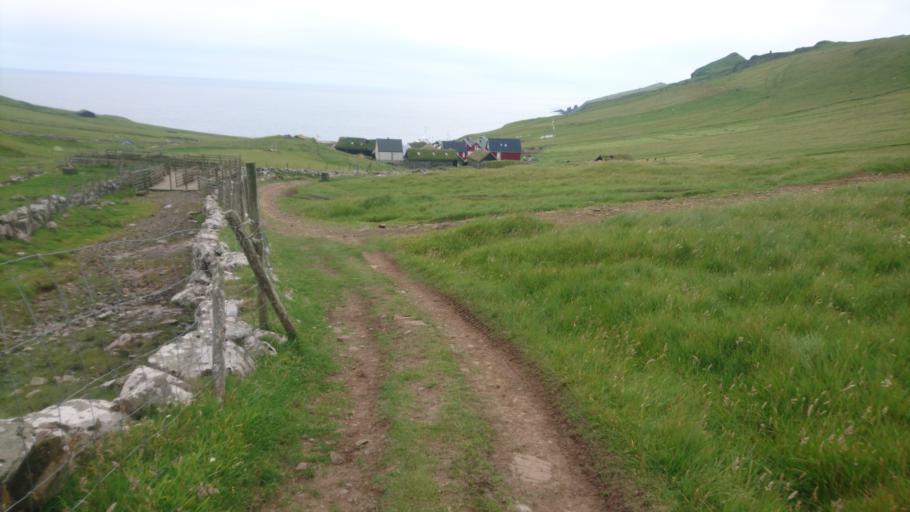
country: FO
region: Vagar
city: Sorvagur
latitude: 62.1054
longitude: -7.6408
